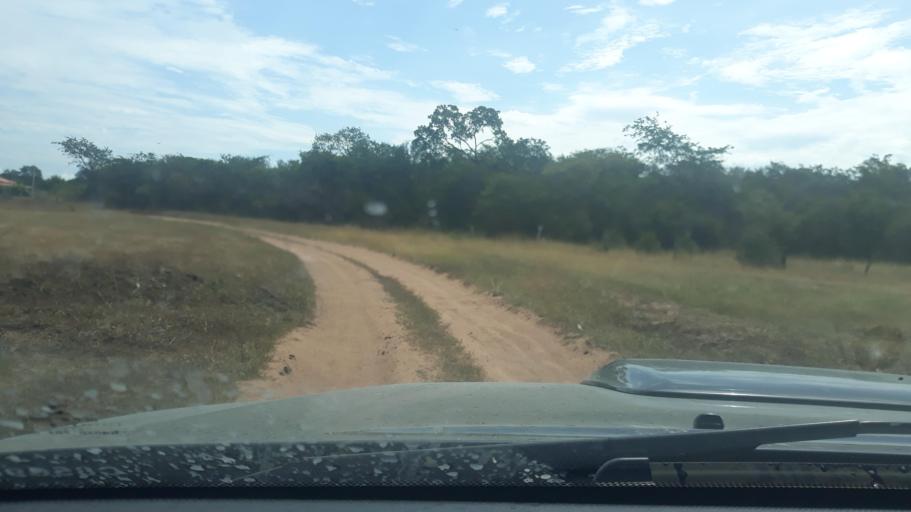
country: BR
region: Bahia
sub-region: Riacho De Santana
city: Riacho de Santana
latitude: -13.8699
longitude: -43.0184
